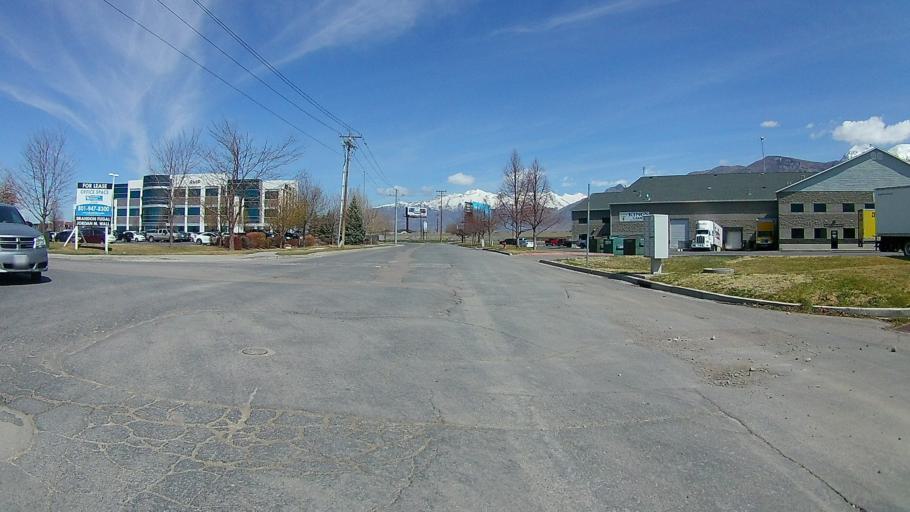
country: US
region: Utah
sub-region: Utah County
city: American Fork
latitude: 40.3513
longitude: -111.7742
